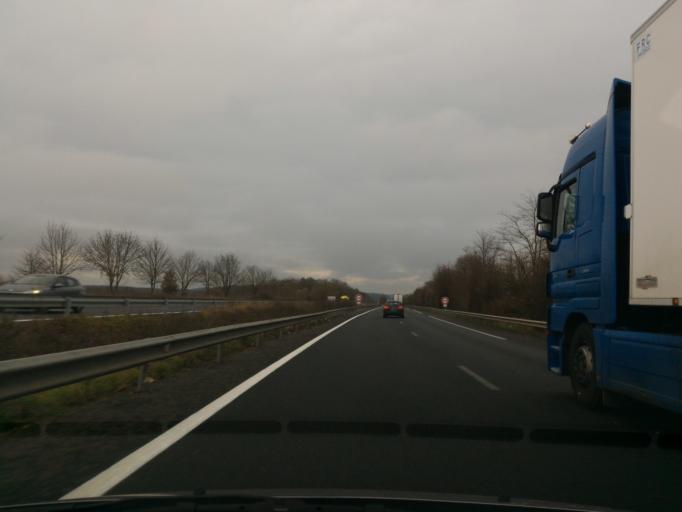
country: FR
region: Poitou-Charentes
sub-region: Departement de la Vienne
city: Fontaine-le-Comte
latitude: 46.5042
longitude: 0.2776
